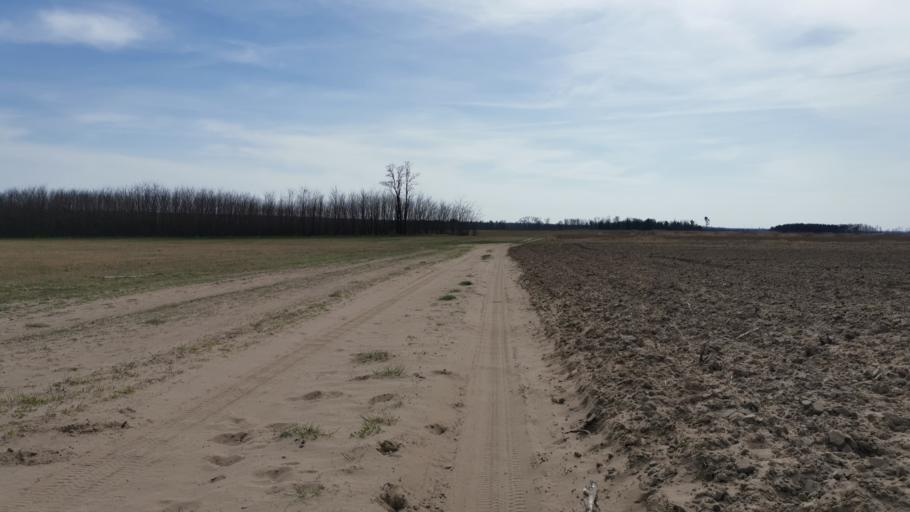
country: SK
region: Trnavsky
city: Gbely
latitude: 48.6716
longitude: 17.1132
